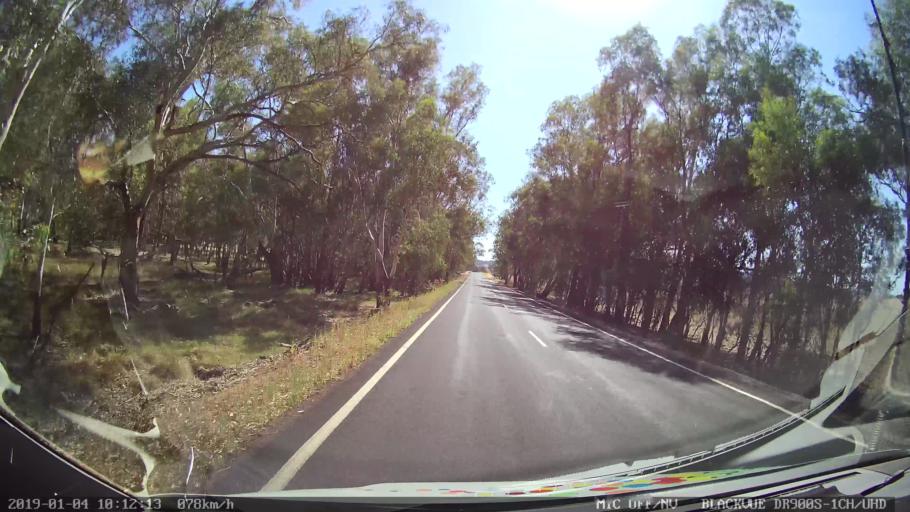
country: AU
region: New South Wales
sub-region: Cabonne
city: Canowindra
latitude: -33.4136
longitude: 148.3921
